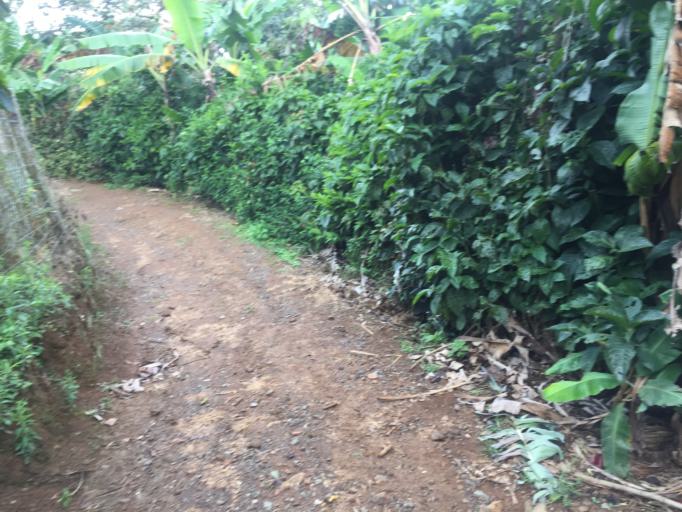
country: CO
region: Valle del Cauca
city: Cali
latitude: 3.4625
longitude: -76.6365
